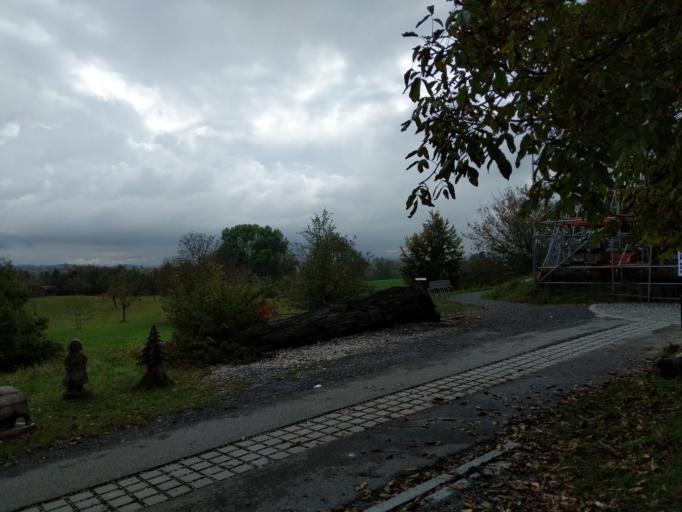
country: DE
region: Bavaria
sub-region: Upper Bavaria
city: Ebersberg
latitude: 48.0888
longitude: 11.9602
